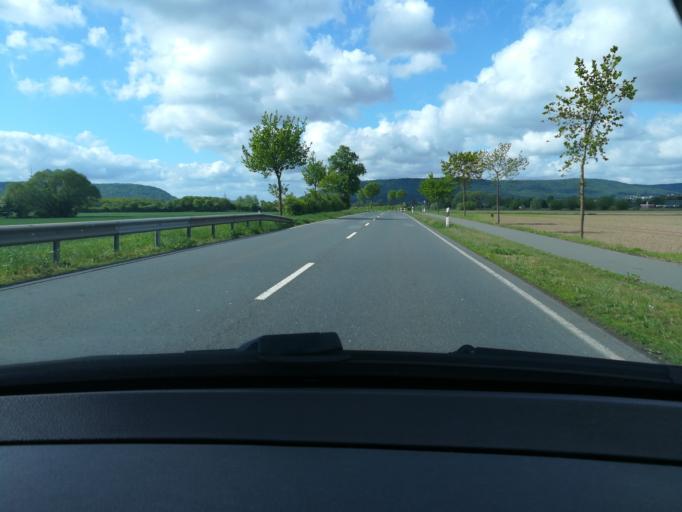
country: DE
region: North Rhine-Westphalia
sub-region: Regierungsbezirk Detmold
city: Minden
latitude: 52.2804
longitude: 8.9285
